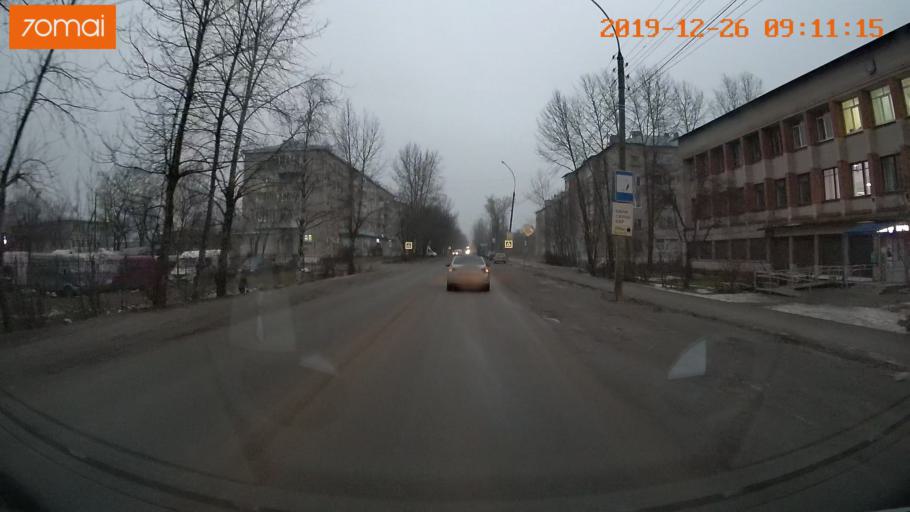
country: RU
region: Vologda
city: Gryazovets
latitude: 58.8750
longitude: 40.2525
